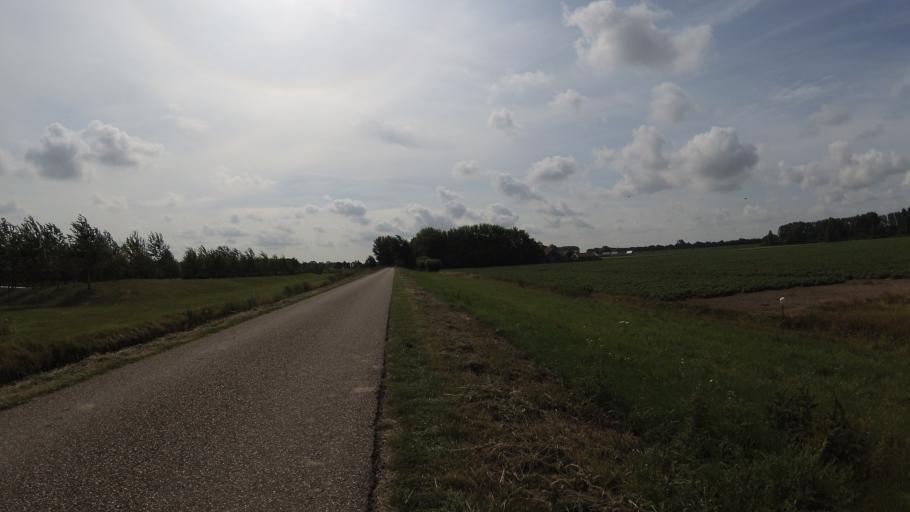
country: NL
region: Zeeland
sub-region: Gemeente Noord-Beveland
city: Kamperland
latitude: 51.5676
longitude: 3.6832
